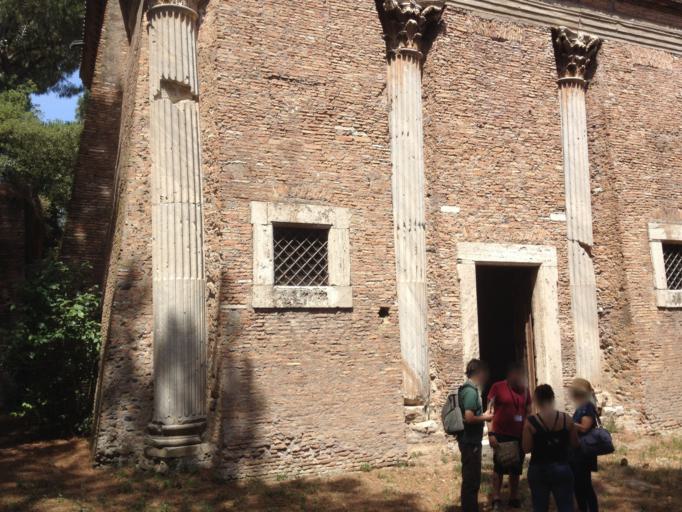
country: IT
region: Latium
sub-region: Citta metropolitana di Roma Capitale
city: Rome
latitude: 41.8578
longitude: 12.5245
